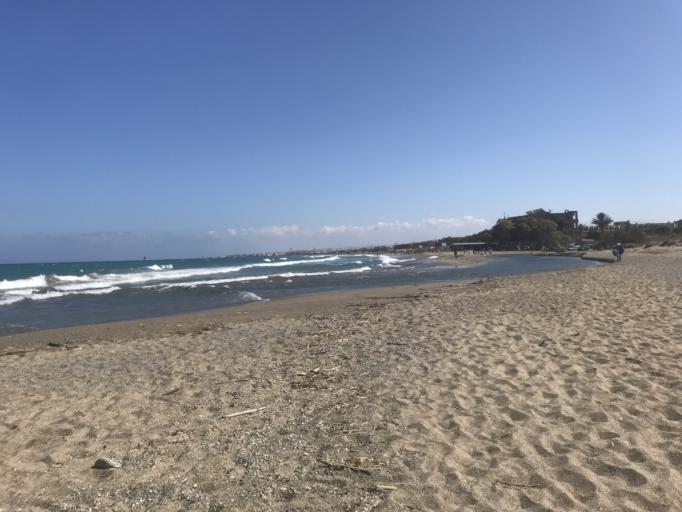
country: GR
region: Crete
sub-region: Nomos Irakleiou
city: Gazi
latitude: 35.3399
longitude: 25.0612
